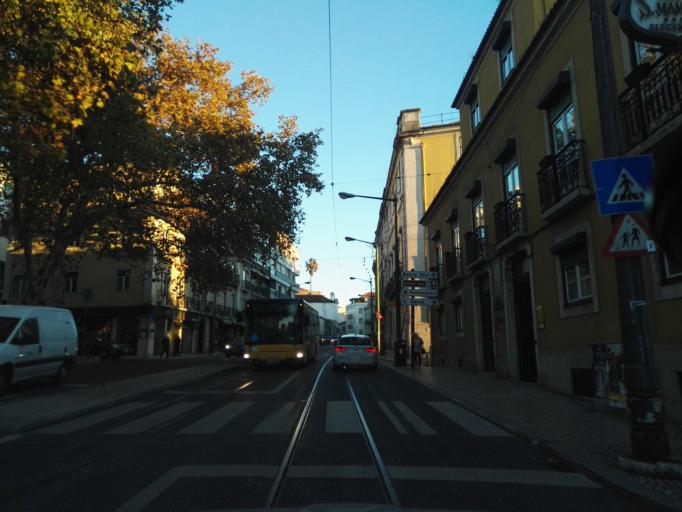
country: PT
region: Lisbon
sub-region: Lisbon
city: Lisbon
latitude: 38.7185
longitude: -9.1528
